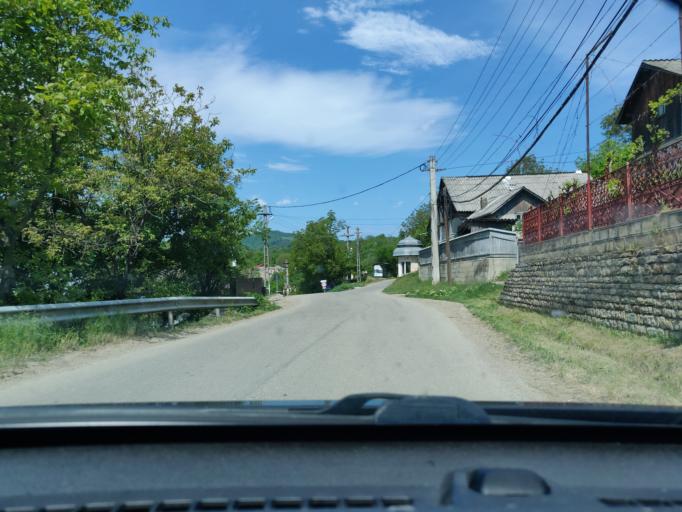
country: RO
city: Vizantea-Manastireasca
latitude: 45.9606
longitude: 26.8232
